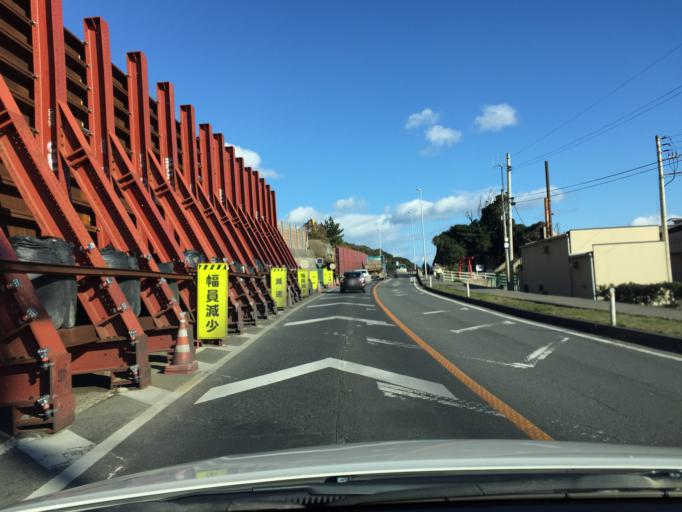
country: JP
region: Fukushima
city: Iwaki
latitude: 37.1124
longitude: 140.9987
